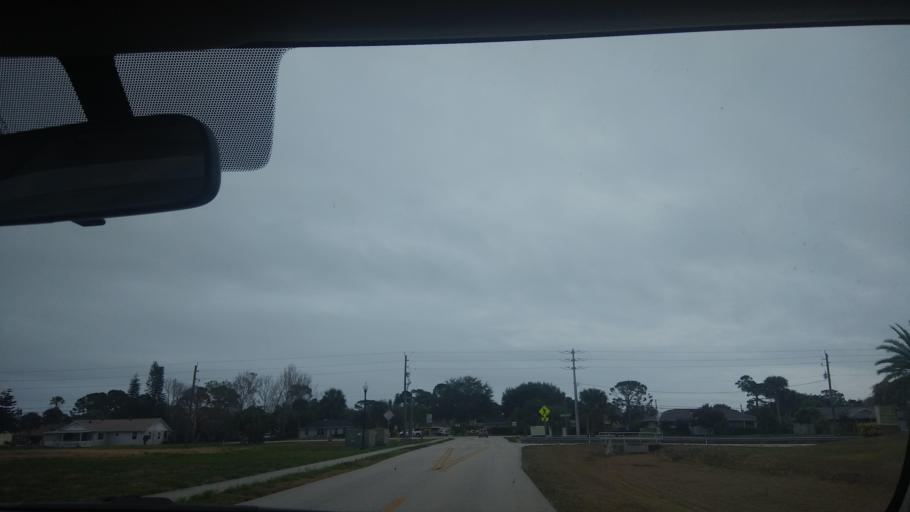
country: US
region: Florida
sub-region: Indian River County
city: Sebastian
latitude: 27.8107
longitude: -80.4869
